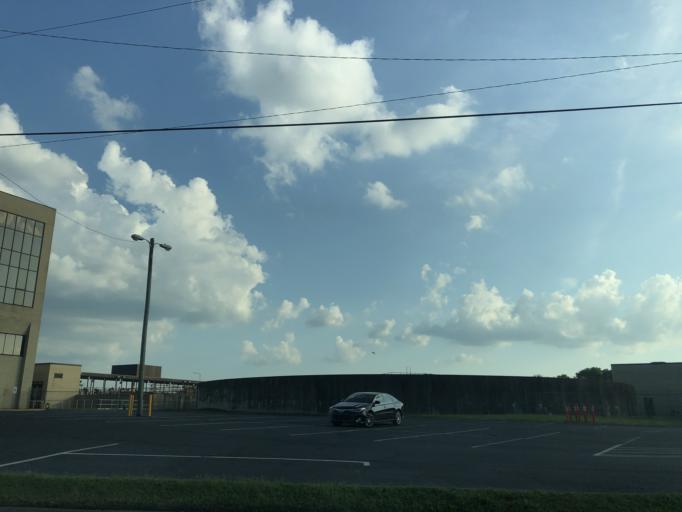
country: US
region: Tennessee
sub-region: Davidson County
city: Nashville
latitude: 36.1868
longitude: -86.7875
